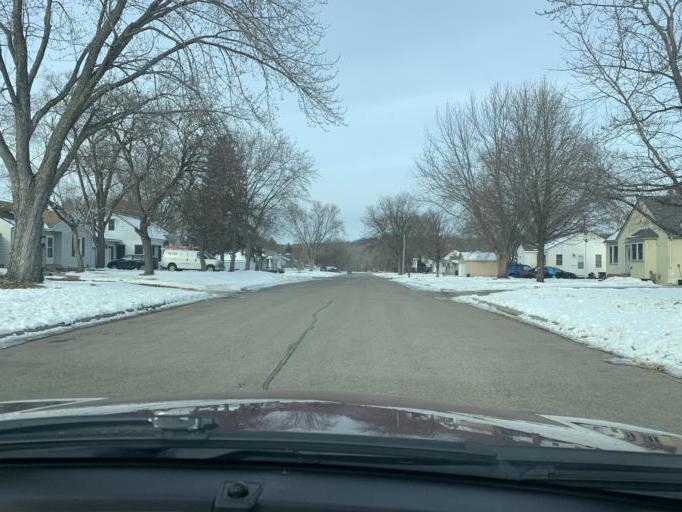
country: US
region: Minnesota
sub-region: Washington County
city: Saint Paul Park
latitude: 44.8378
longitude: -92.9785
